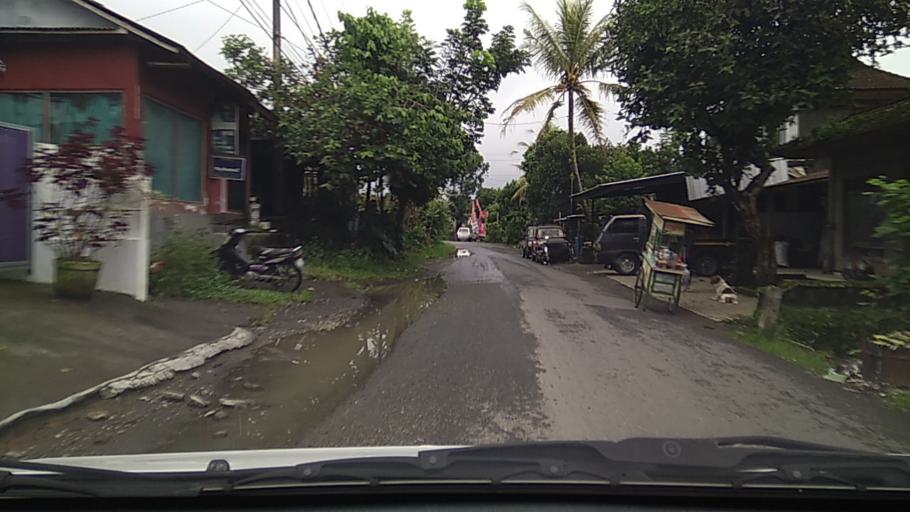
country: ID
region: Bali
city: Banjar Manukayaanyar
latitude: -8.4175
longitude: 115.2986
